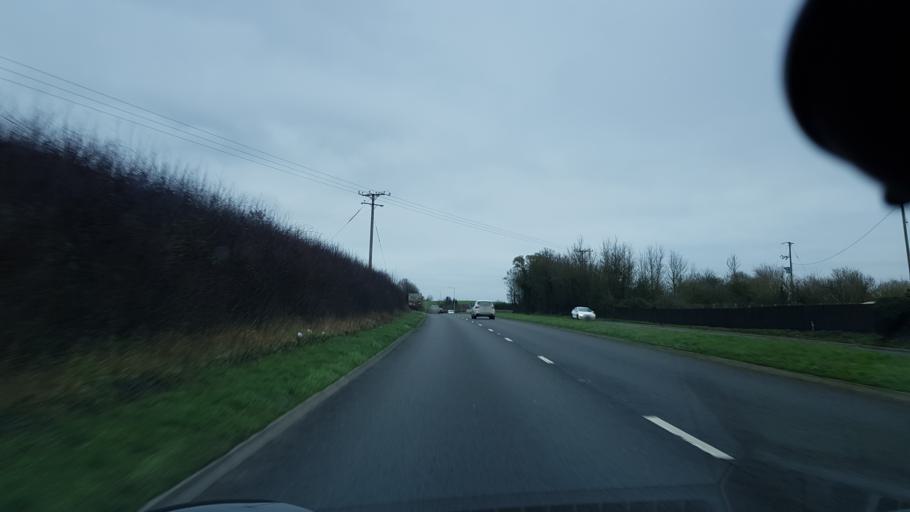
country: GB
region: England
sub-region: Somerset
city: Creech Saint Michael
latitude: 51.0048
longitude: -3.0289
